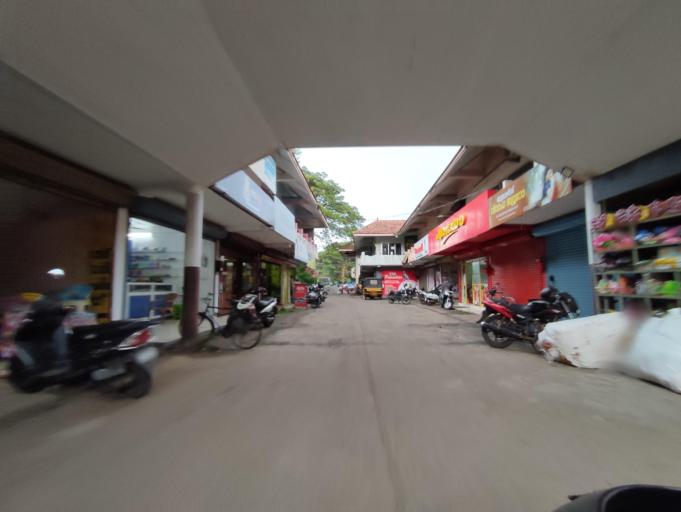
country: IN
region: Kerala
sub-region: Alappuzha
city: Vayalar
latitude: 9.6875
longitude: 76.3392
